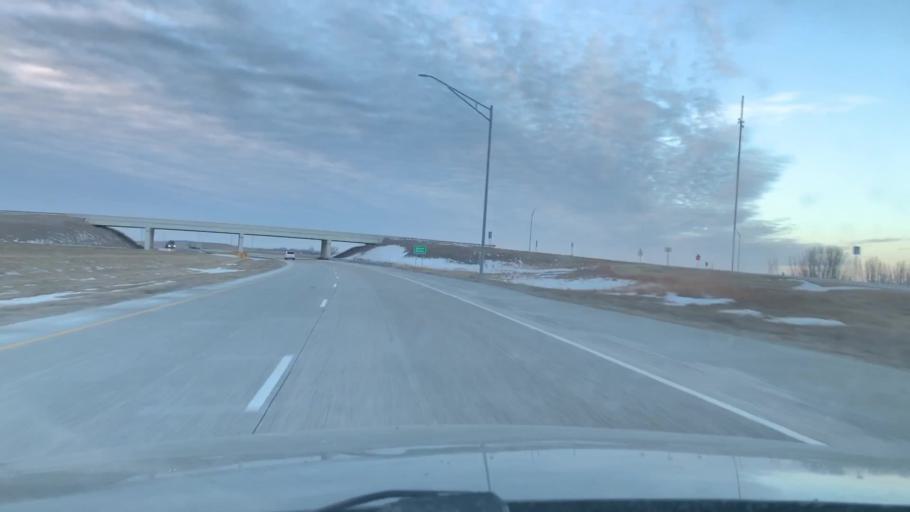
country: US
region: North Dakota
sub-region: Barnes County
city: Valley City
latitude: 46.9179
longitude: -97.6806
